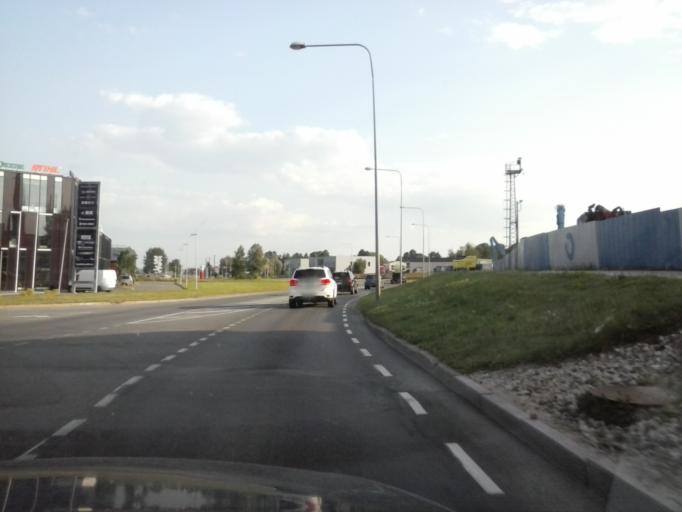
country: EE
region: Tartu
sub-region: Tartu linn
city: Tartu
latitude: 58.3589
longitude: 26.7413
